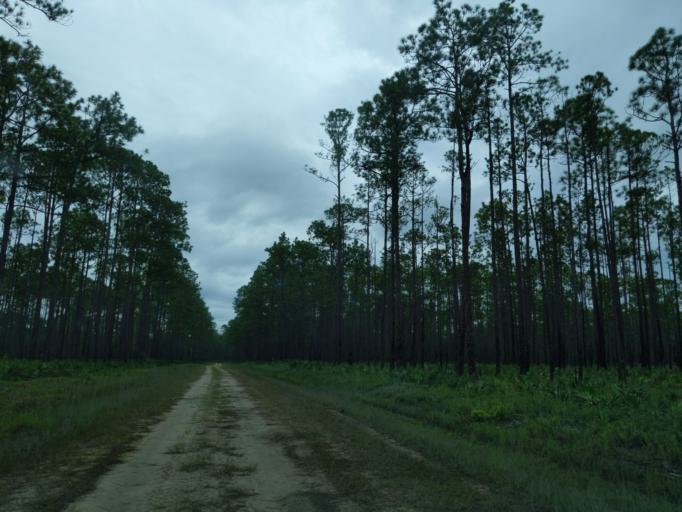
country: US
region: Florida
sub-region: Gadsden County
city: Midway
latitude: 30.3694
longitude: -84.4856
